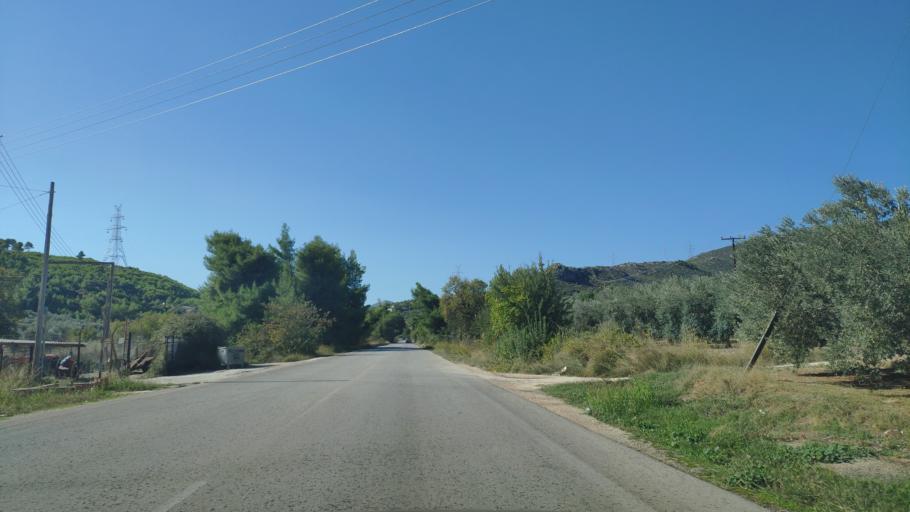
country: GR
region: Peloponnese
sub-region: Nomos Korinthias
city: Khiliomodhi
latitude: 37.8331
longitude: 22.8928
